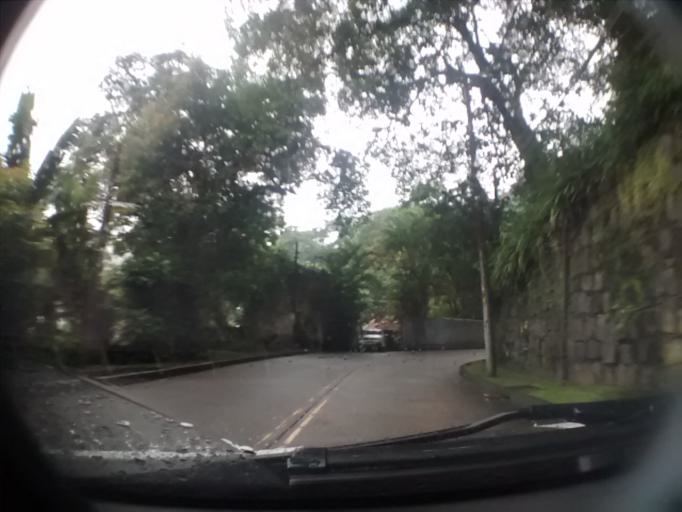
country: BR
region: Rio de Janeiro
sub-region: Rio De Janeiro
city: Rio de Janeiro
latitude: -22.9720
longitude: -43.2808
